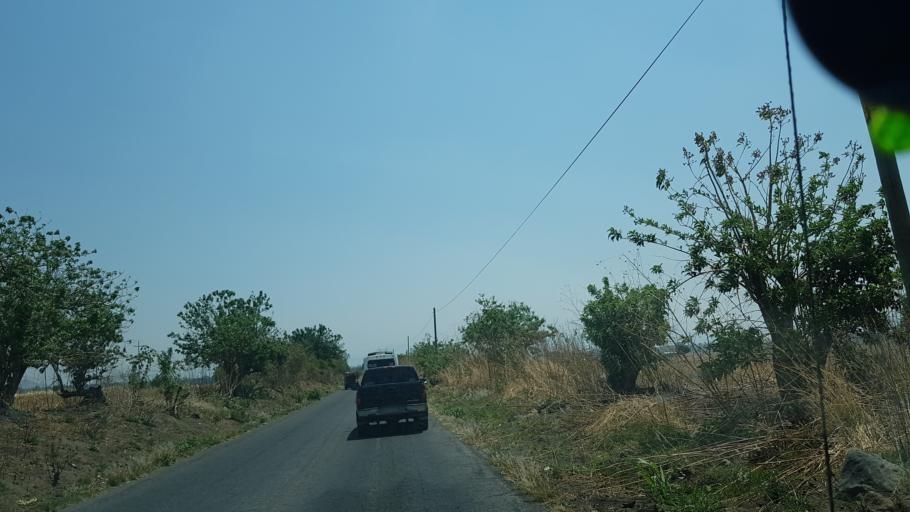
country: MX
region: Puebla
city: Tochimilco
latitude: 18.8883
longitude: -98.5332
